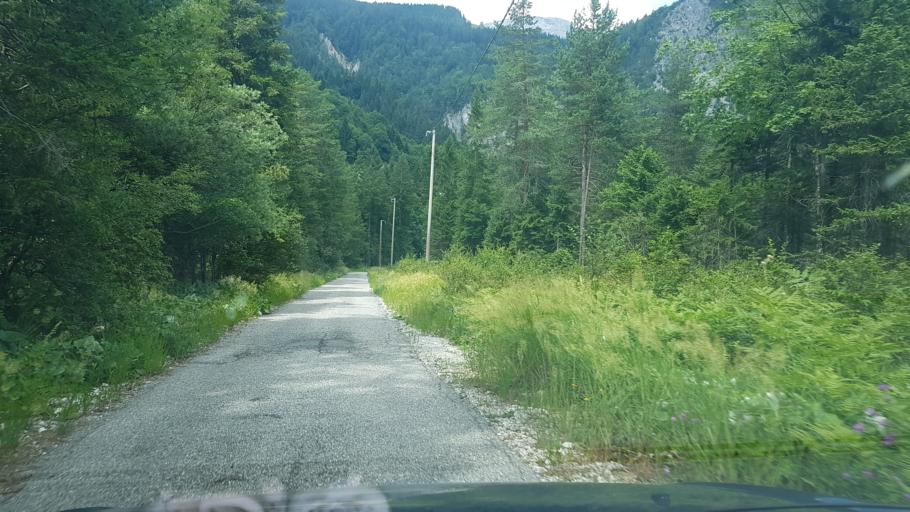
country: IT
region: Friuli Venezia Giulia
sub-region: Provincia di Udine
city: Pontebba
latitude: 46.5011
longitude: 13.2537
